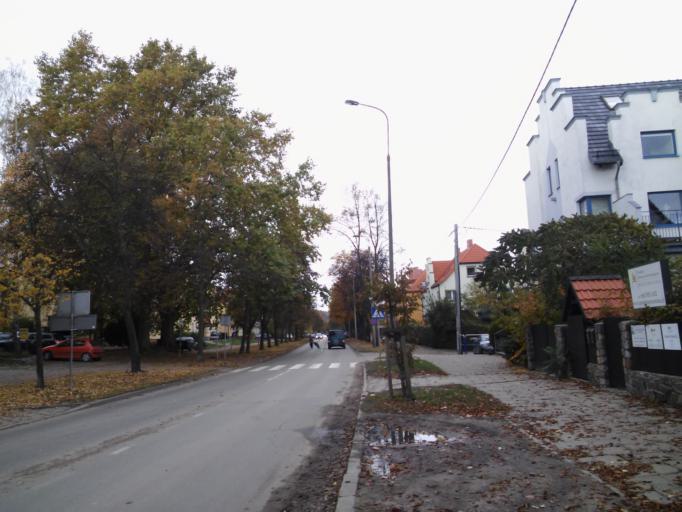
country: PL
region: Pomeranian Voivodeship
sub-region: Sopot
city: Sopot
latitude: 54.3832
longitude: 18.5848
